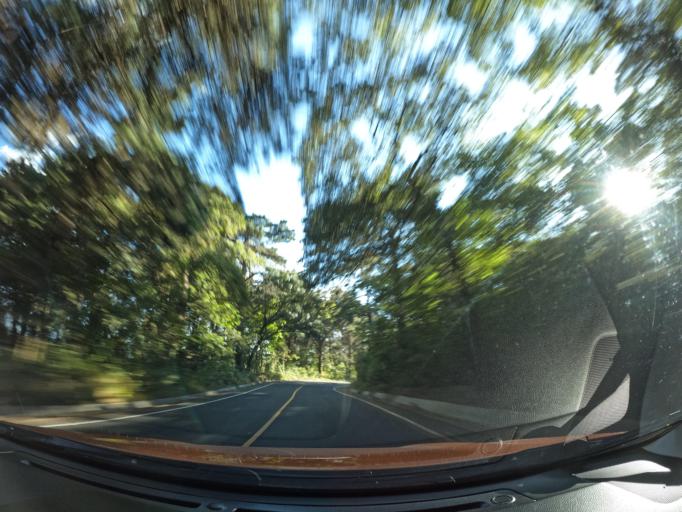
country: GT
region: Escuintla
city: Palin
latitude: 14.4593
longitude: -90.6943
